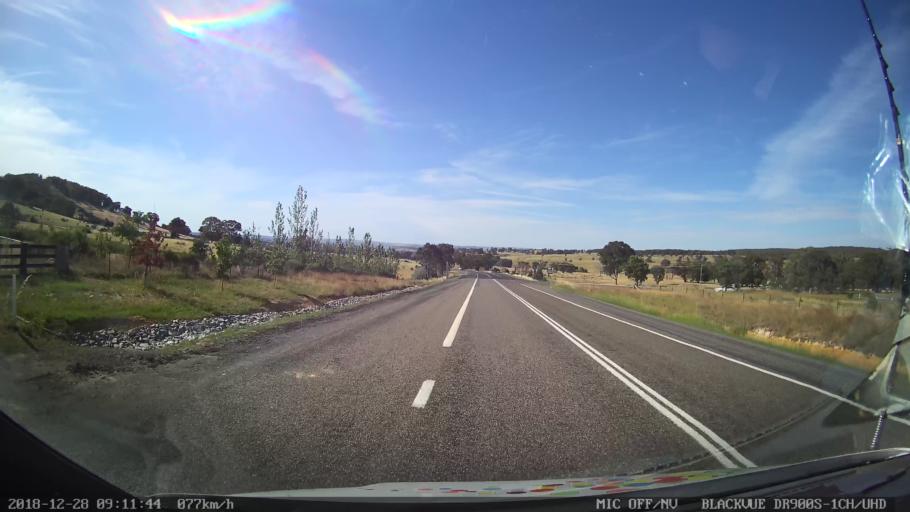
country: AU
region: New South Wales
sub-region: Upper Lachlan Shire
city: Crookwell
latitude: -34.2470
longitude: 149.3386
